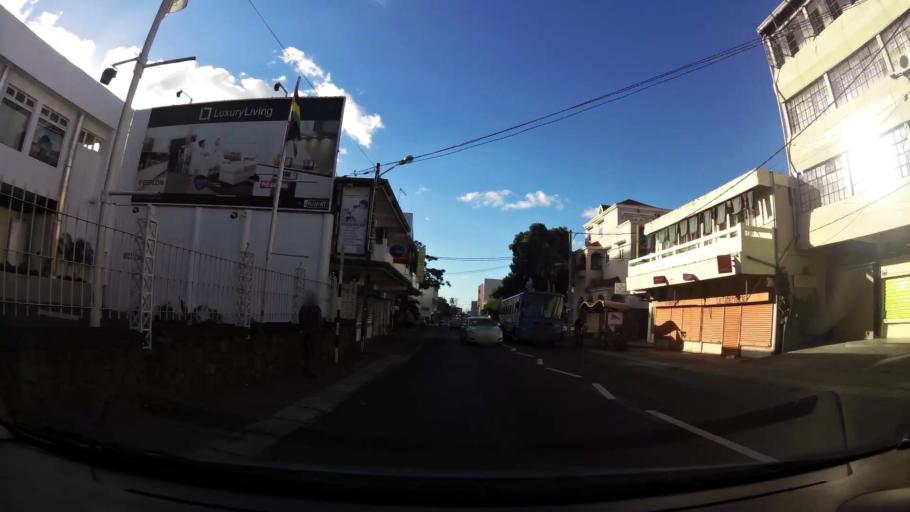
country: MU
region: Plaines Wilhems
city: Ebene
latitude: -20.2291
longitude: 57.4677
